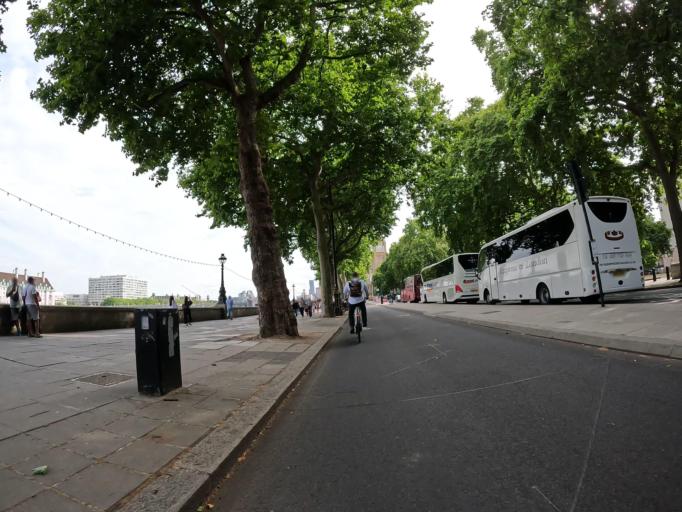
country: GB
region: England
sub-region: Greater London
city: Bromley
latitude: 51.4173
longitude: 0.0210
